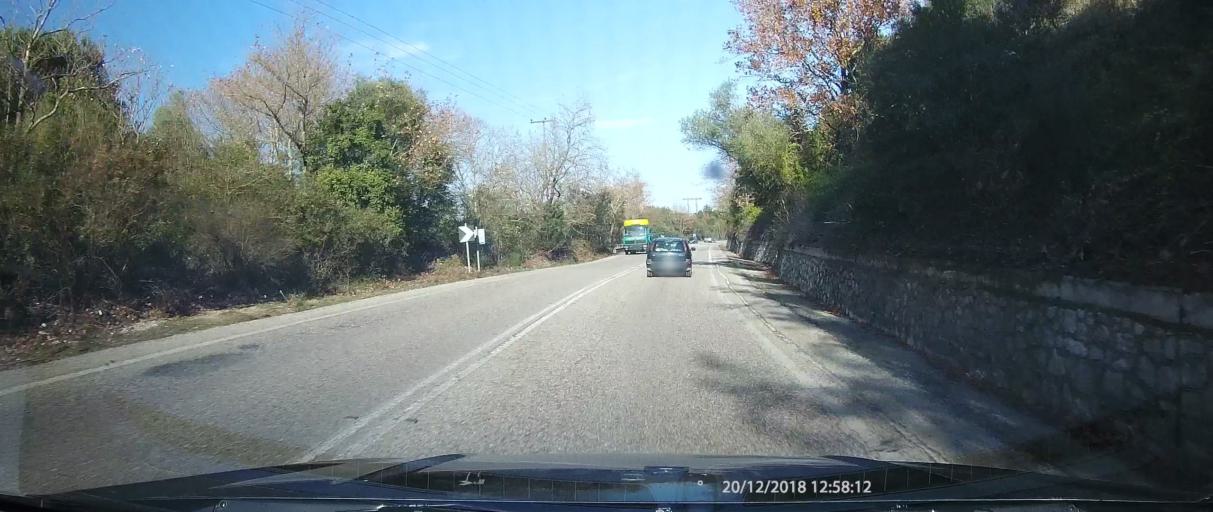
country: GR
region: West Greece
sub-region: Nomos Aitolias kai Akarnanias
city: Pappadhatai
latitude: 38.5342
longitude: 21.3753
